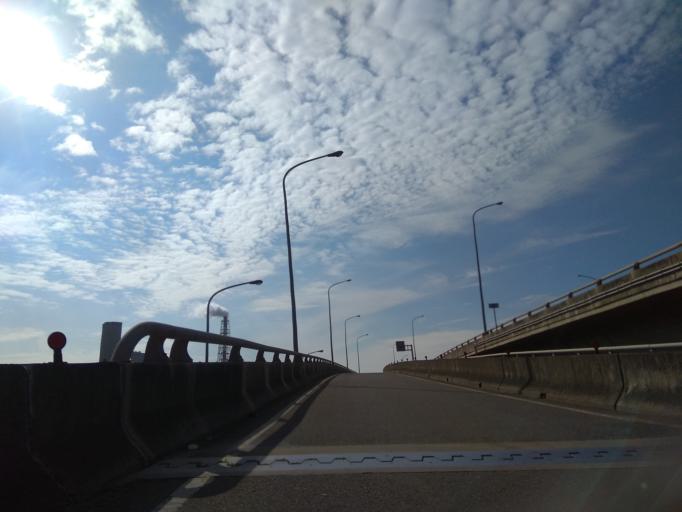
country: TW
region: Taiwan
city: Taoyuan City
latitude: 25.0823
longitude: 121.1787
